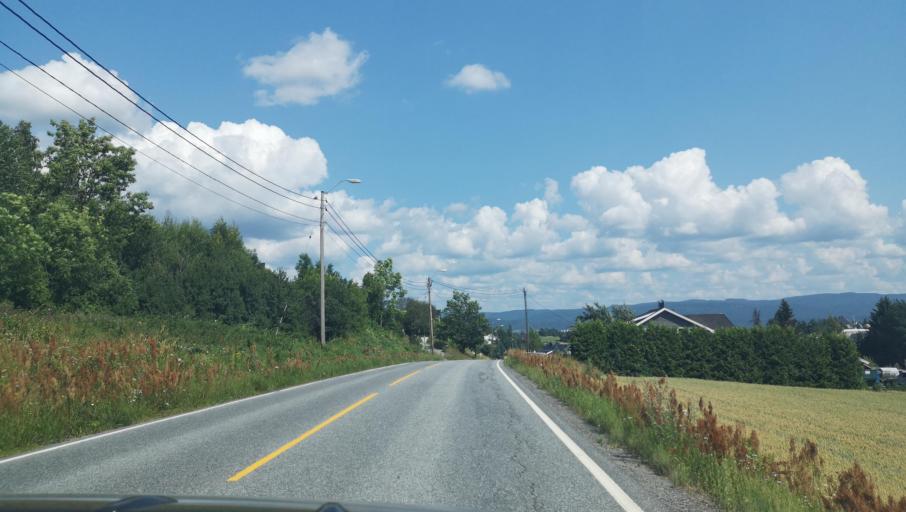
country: NO
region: Buskerud
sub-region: Ovre Eiker
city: Hokksund
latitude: 59.7318
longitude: 9.8467
